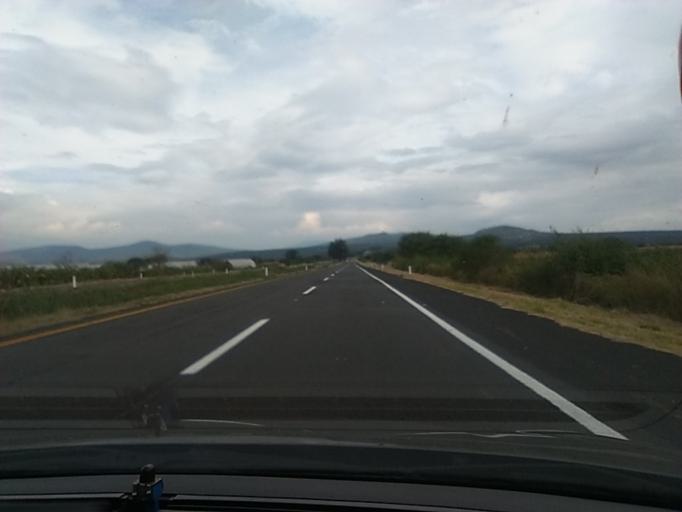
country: MX
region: Michoacan
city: Vistahermosa de Negrete
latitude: 20.2618
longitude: -102.4303
